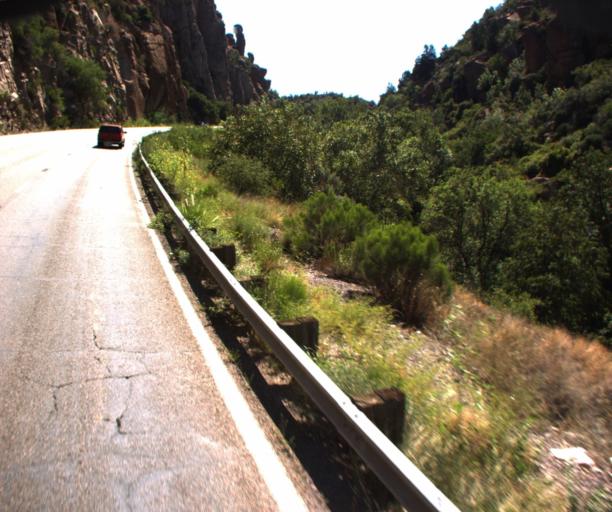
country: US
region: Arizona
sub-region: Pinal County
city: Superior
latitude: 33.3099
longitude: -111.0671
